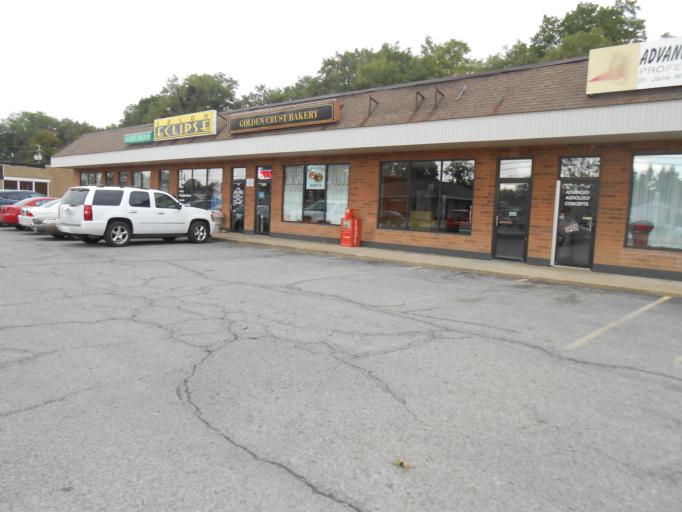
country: US
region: Ohio
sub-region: Lake County
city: Mentor
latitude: 41.6750
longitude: -81.3234
